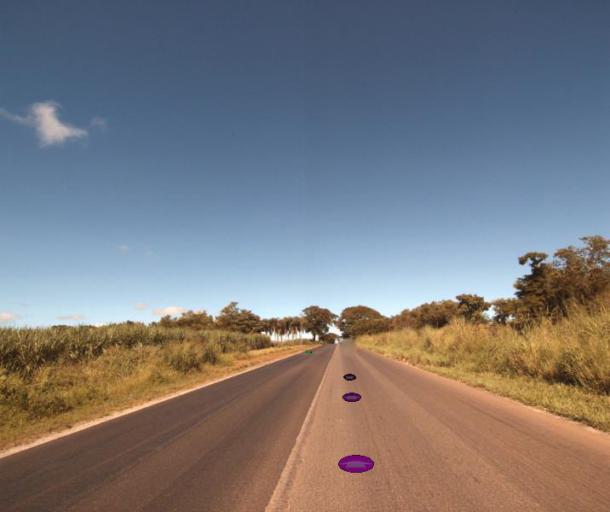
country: BR
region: Goias
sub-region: Itapaci
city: Itapaci
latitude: -15.1288
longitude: -49.5109
